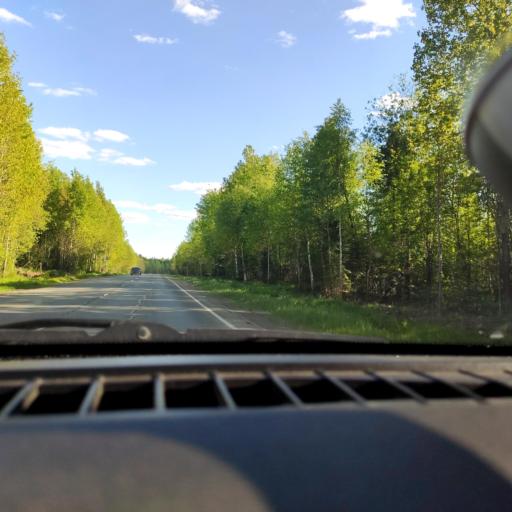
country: RU
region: Perm
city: Polazna
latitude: 58.2726
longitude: 56.1667
